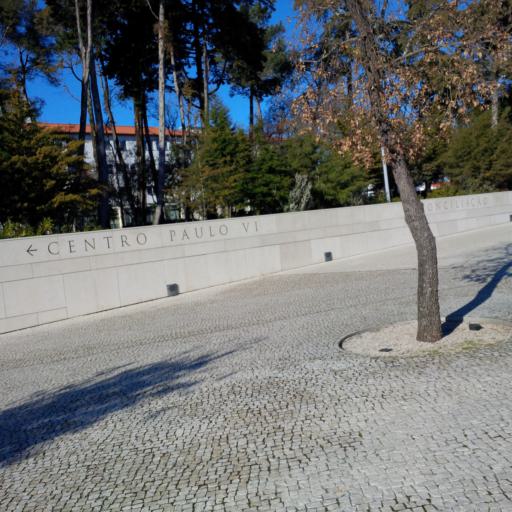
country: PT
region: Santarem
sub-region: Ourem
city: Fatima
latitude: 39.6301
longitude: -8.6757
